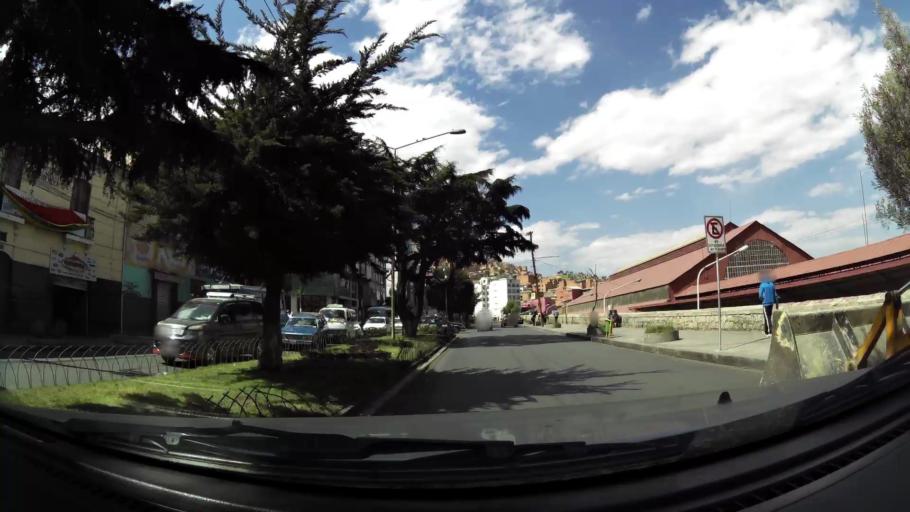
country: BO
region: La Paz
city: La Paz
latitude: -16.4883
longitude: -68.1421
